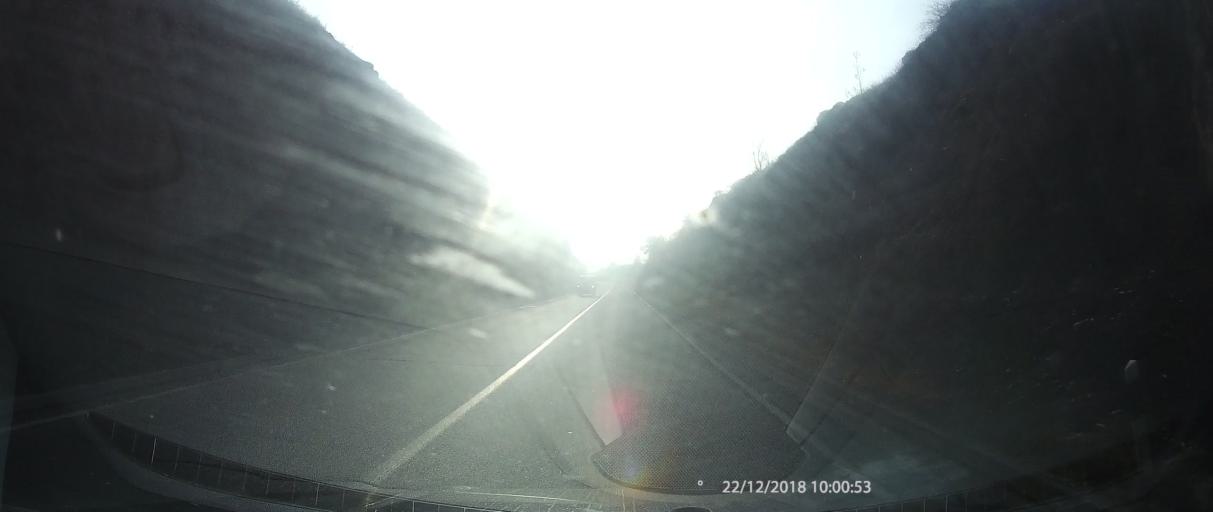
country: MK
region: Opstina Rankovce
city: Rankovce
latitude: 42.1479
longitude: 21.9874
